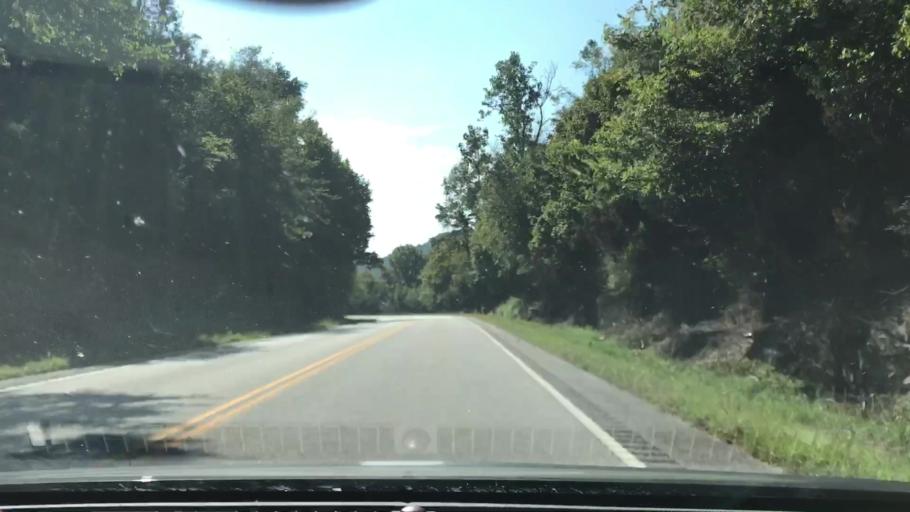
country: US
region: Tennessee
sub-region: Jackson County
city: Gainesboro
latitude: 36.3612
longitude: -85.7524
